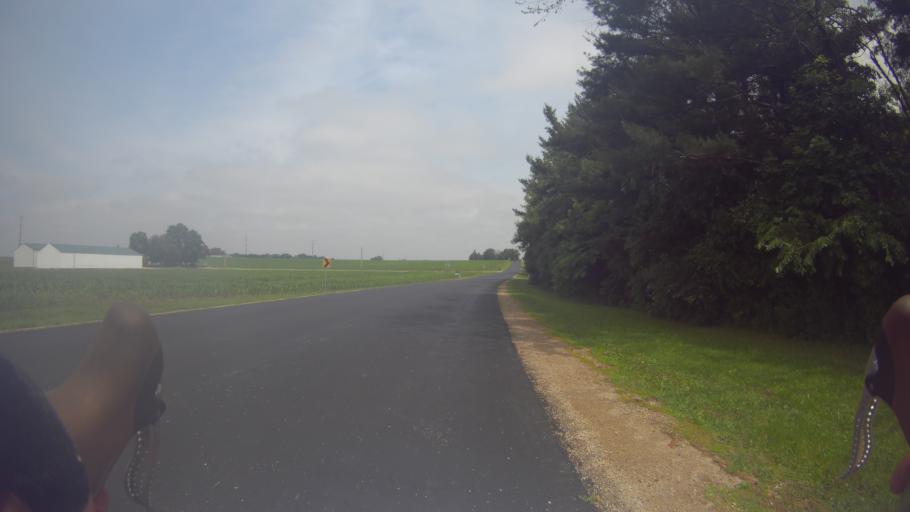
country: US
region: Wisconsin
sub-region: Rock County
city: Edgerton
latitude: 42.8969
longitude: -89.0426
